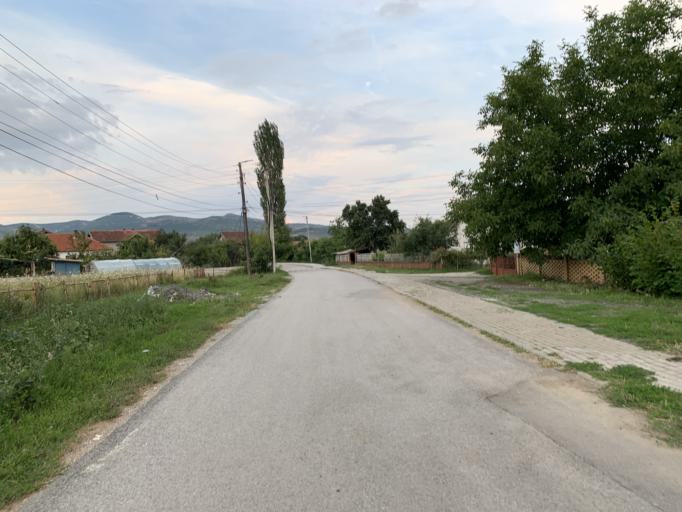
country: XK
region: Pristina
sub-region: Komuna e Prishtines
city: Pristina
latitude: 42.6006
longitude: 21.1876
